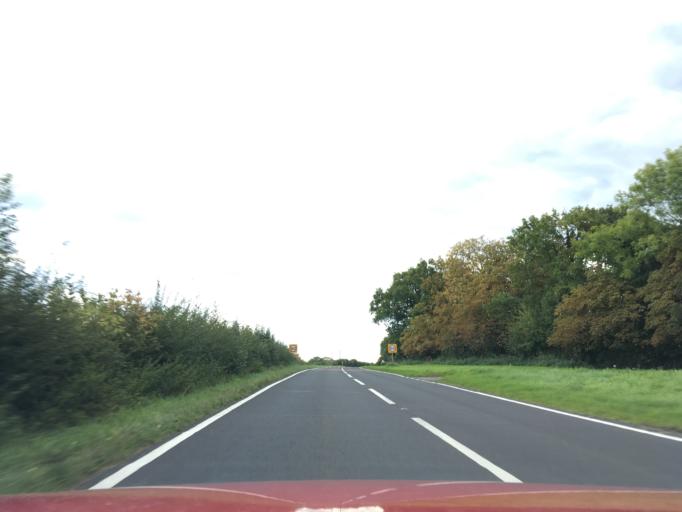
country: GB
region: England
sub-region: South Gloucestershire
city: Alveston
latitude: 51.5778
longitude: -2.5364
